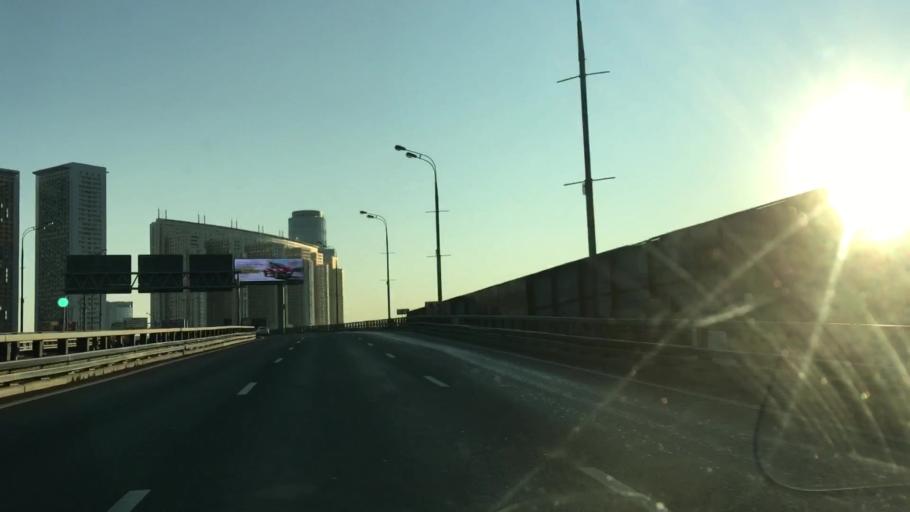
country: RU
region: Moskovskaya
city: Presnenskiy
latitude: 55.7694
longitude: 37.5410
